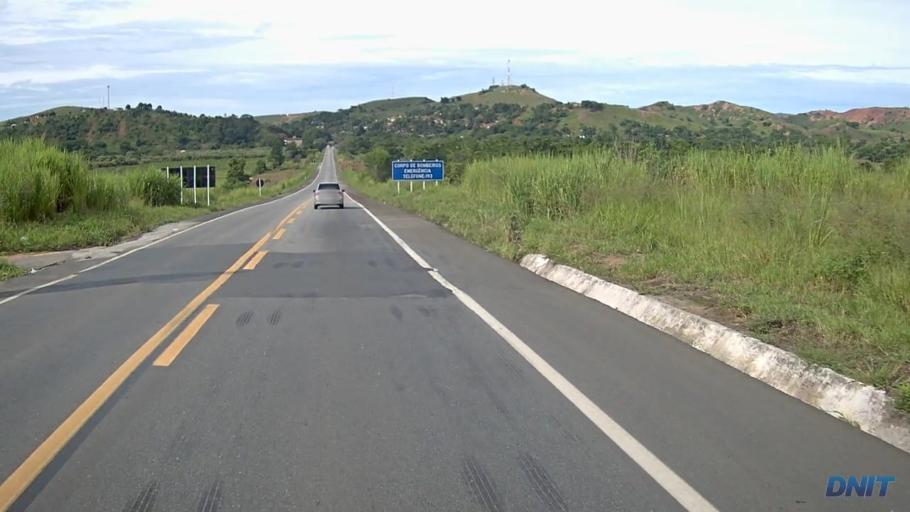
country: BR
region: Minas Gerais
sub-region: Belo Oriente
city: Belo Oriente
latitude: -19.2401
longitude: -42.3339
